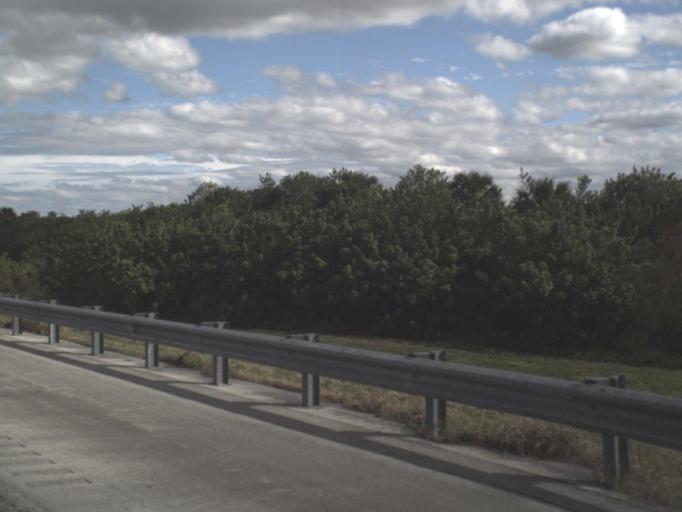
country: US
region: Florida
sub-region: Saint Lucie County
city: Lakewood Park
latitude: 27.4848
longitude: -80.5104
